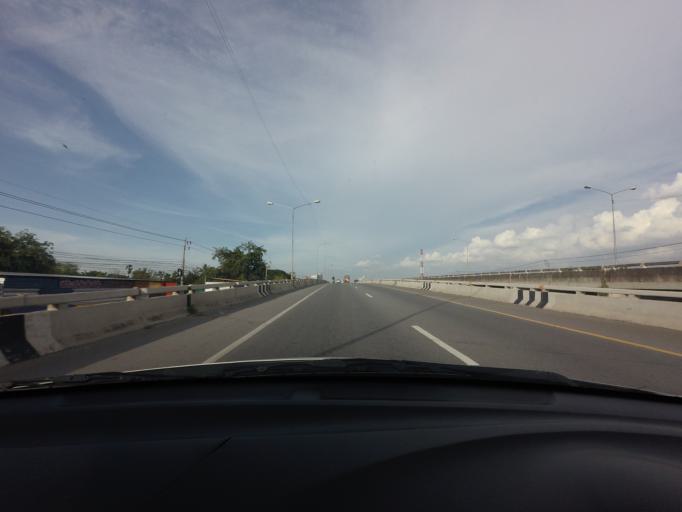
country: TH
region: Nonthaburi
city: Bang Bua Thong
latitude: 13.9482
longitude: 100.4435
